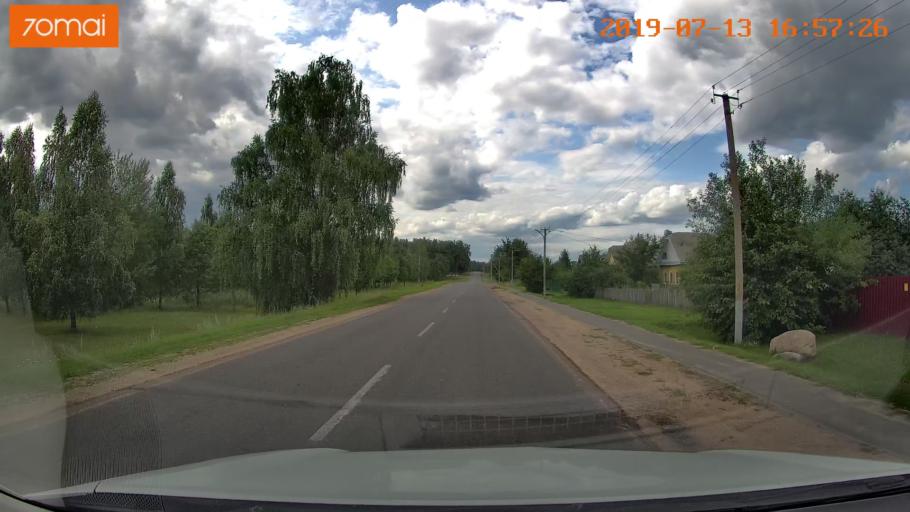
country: BY
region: Mogilev
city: Kirawsk
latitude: 53.2799
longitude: 29.4516
